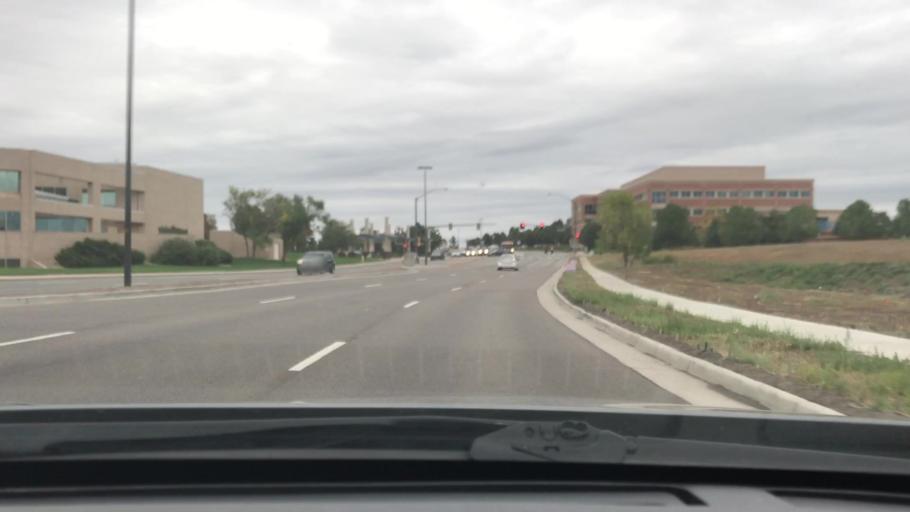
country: US
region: Colorado
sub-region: Adams County
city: Aurora
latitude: 39.7105
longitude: -104.8164
